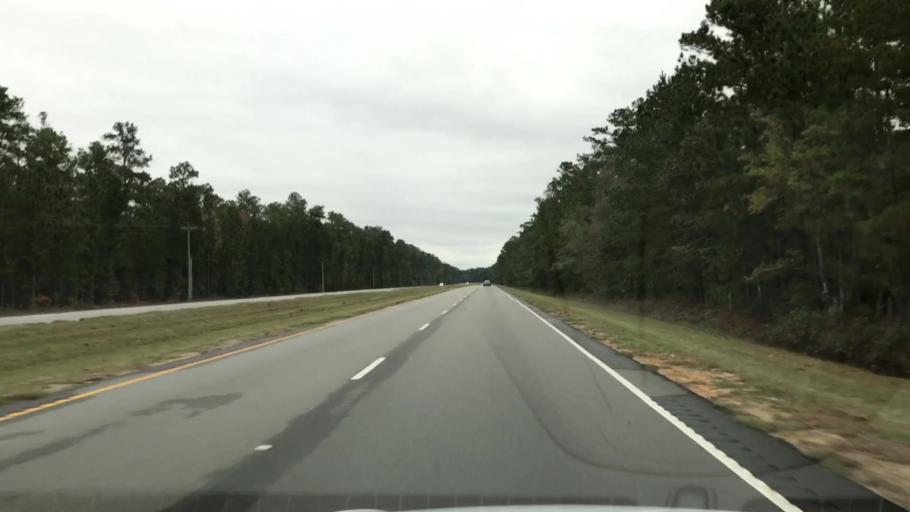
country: US
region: South Carolina
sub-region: Georgetown County
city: Georgetown
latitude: 33.2647
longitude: -79.3622
